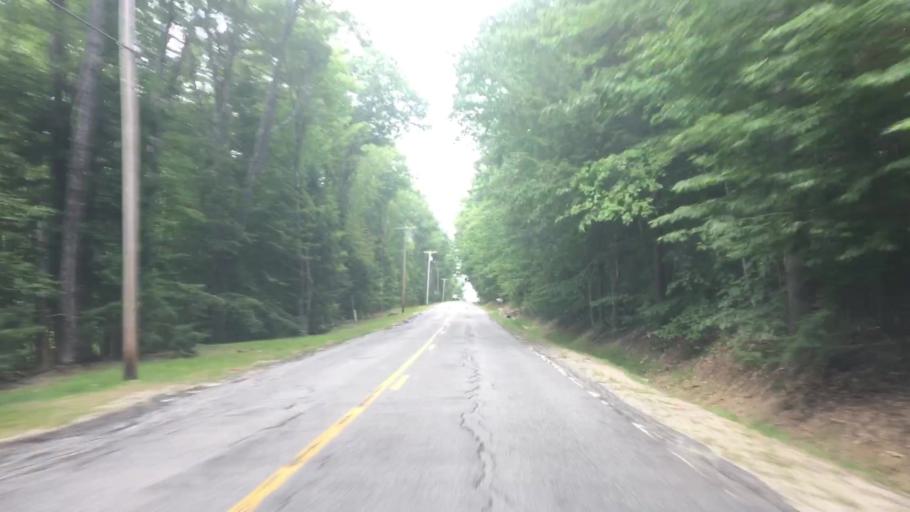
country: US
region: Maine
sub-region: Oxford County
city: Oxford
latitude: 44.0190
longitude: -70.5277
